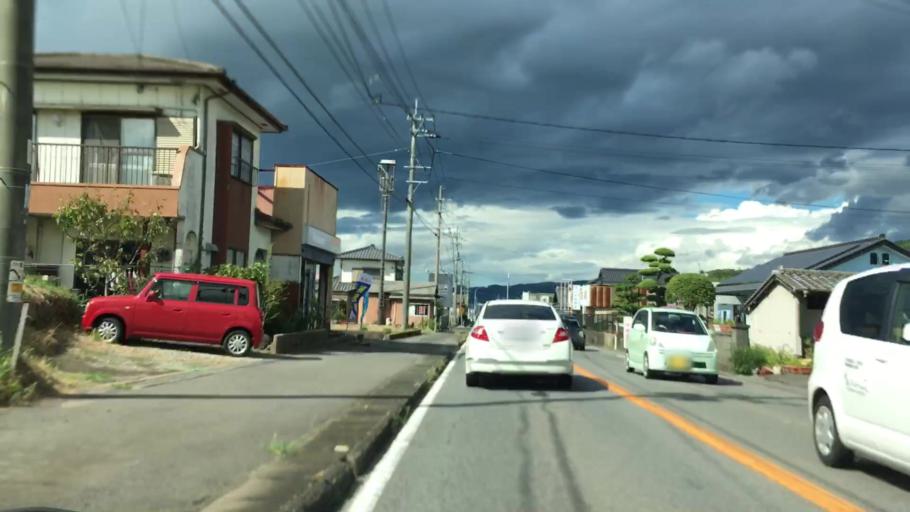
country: JP
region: Saga Prefecture
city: Imaricho-ko
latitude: 33.2434
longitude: 129.8506
